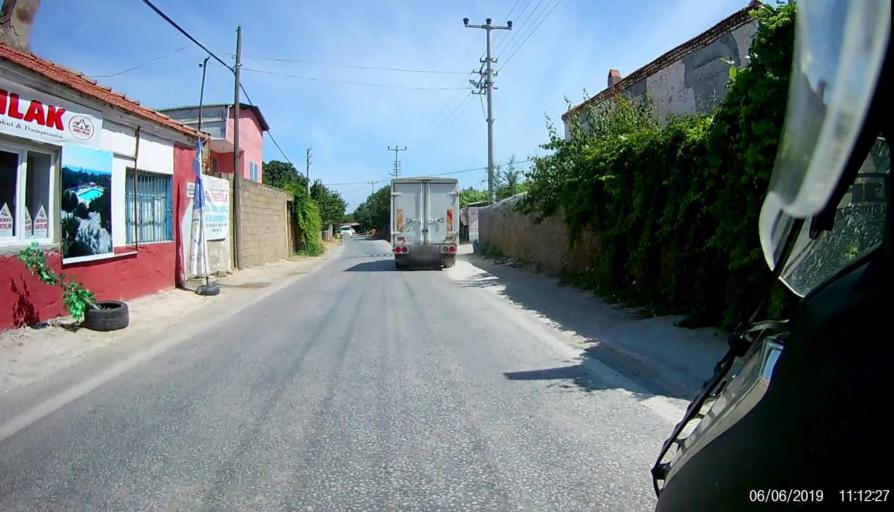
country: TR
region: Canakkale
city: Gulpinar
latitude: 39.6108
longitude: 26.1862
